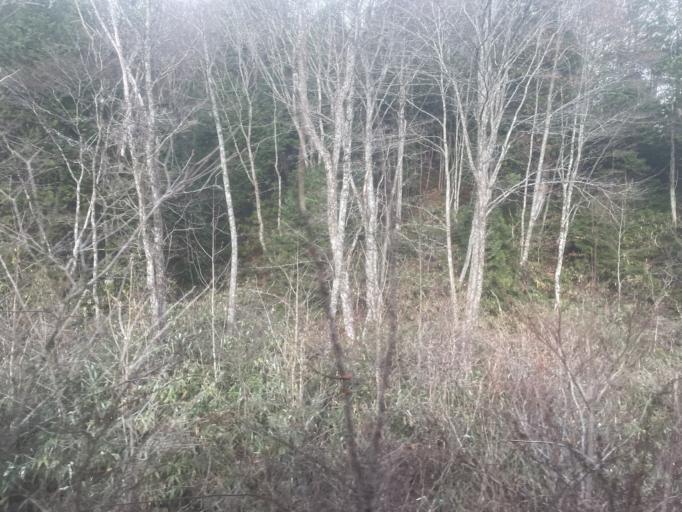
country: JP
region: Aomori
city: Goshogawara
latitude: 41.0780
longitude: 140.5332
